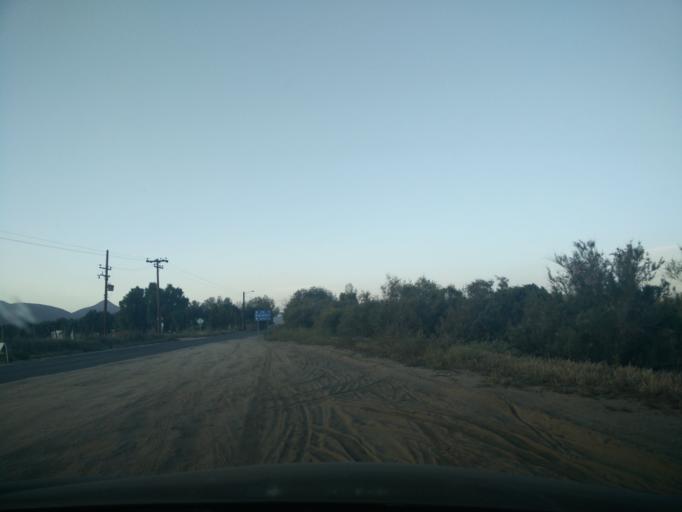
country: MX
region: Baja California
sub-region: Ensenada
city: Rancho Verde
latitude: 32.0565
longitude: -116.6481
